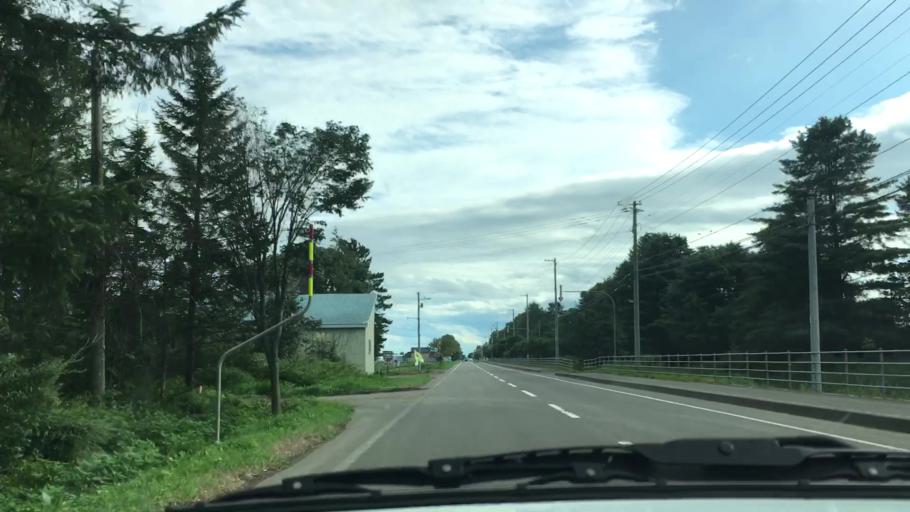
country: JP
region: Hokkaido
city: Otofuke
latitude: 43.2481
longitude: 143.2986
